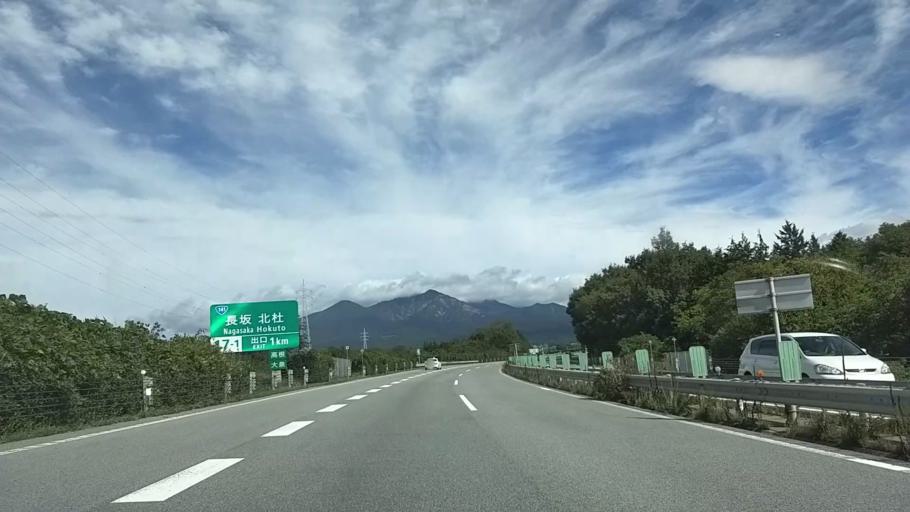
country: JP
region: Yamanashi
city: Nirasaki
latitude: 35.8263
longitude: 138.3927
